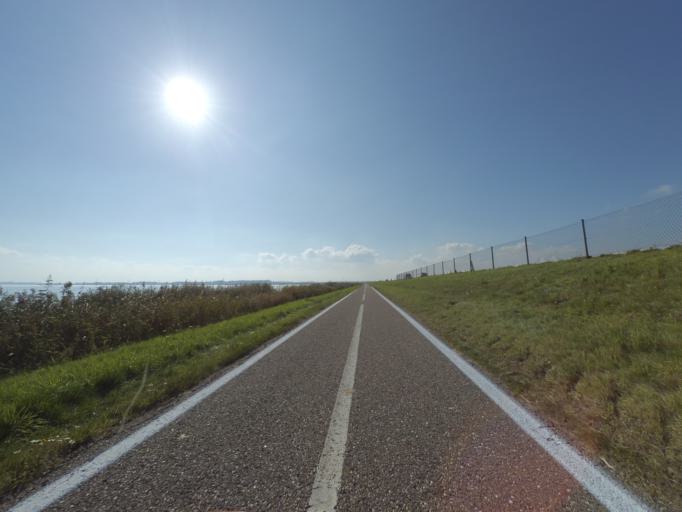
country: NL
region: Flevoland
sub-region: Gemeente Zeewolde
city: Zeewolde
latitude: 52.3558
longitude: 5.5461
